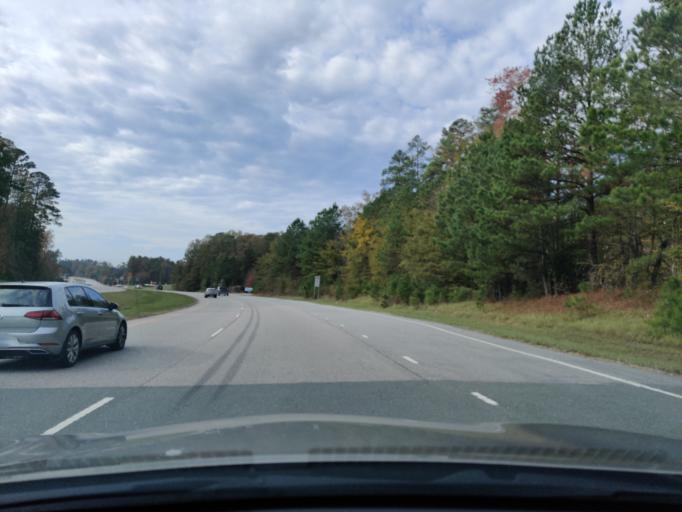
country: US
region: North Carolina
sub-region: Wake County
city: Morrisville
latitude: 35.8695
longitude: -78.8687
